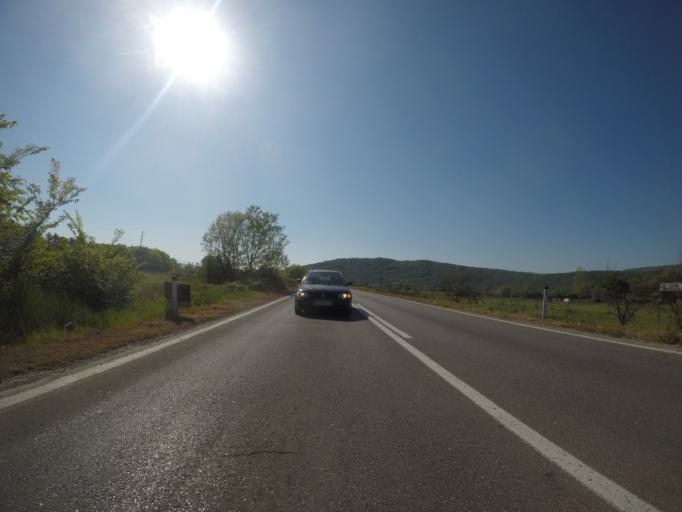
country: ME
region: Danilovgrad
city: Danilovgrad
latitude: 42.5159
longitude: 19.1243
